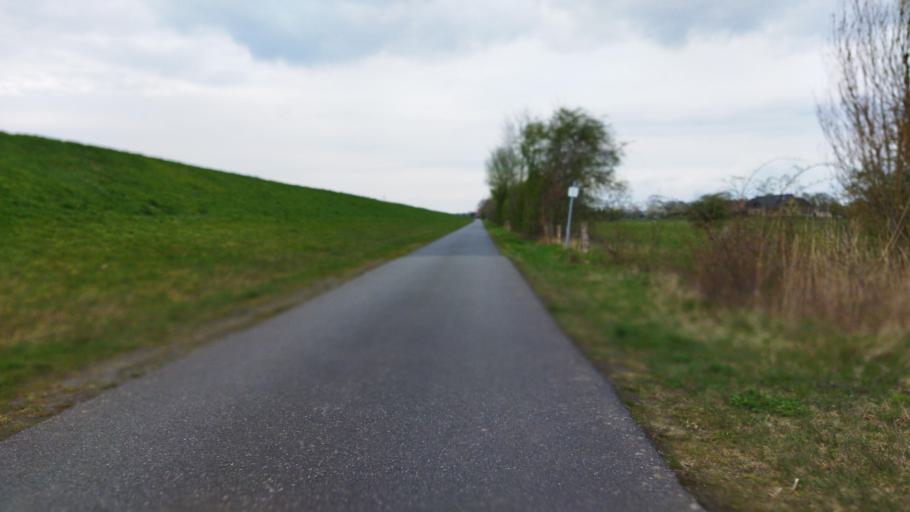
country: DE
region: Lower Saxony
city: Langwedel
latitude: 52.9766
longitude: 9.1392
